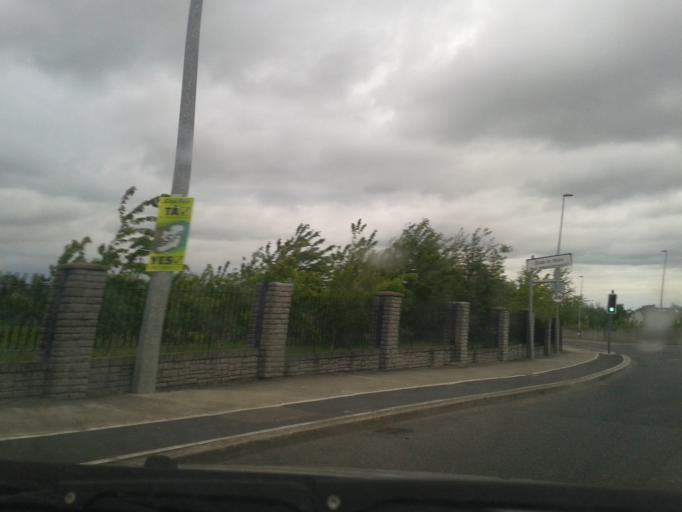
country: IE
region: Leinster
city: Lucan
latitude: 53.3379
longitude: -6.4303
